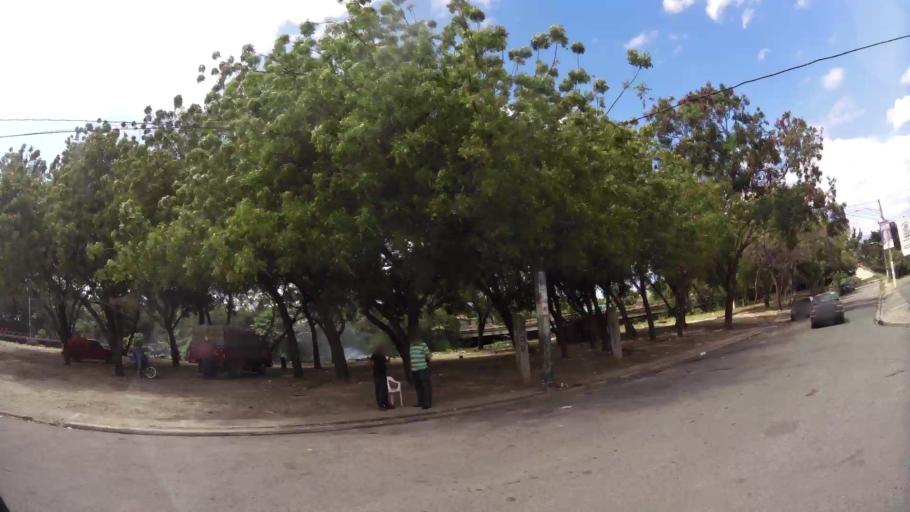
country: DO
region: San Cristobal
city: San Cristobal
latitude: 18.4256
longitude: -70.1157
